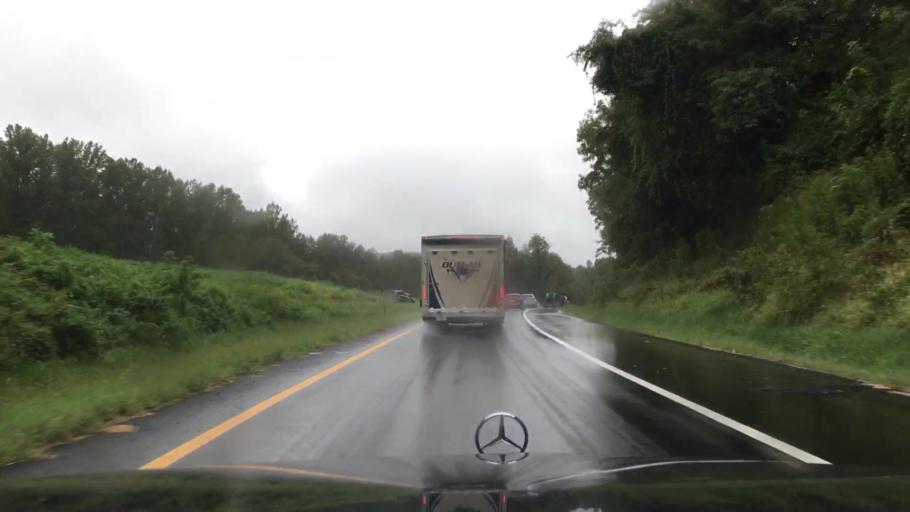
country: US
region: Virginia
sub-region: City of Charlottesville
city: Charlottesville
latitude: 38.0205
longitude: -78.4330
